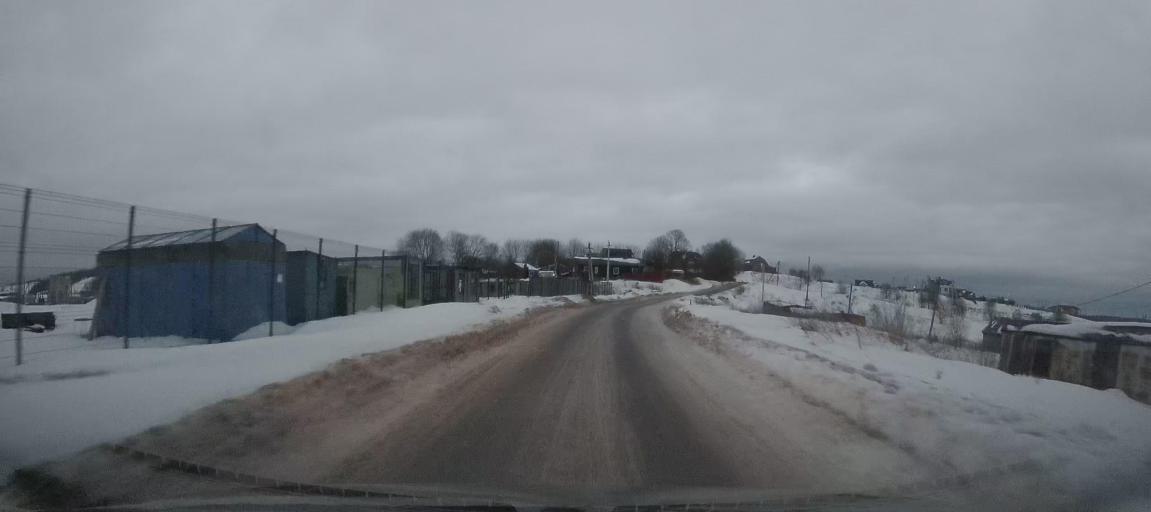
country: RU
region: Leningrad
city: Taytsy
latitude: 59.6962
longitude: 30.1432
